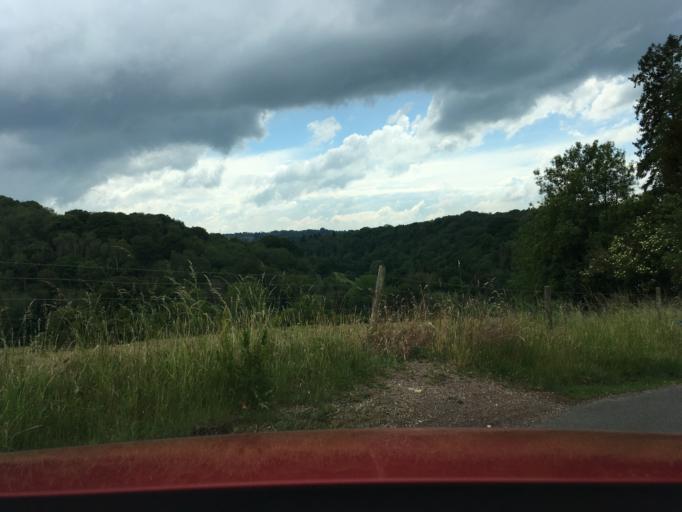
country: GB
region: England
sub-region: Gloucestershire
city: Shurdington
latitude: 51.7930
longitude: -2.0767
